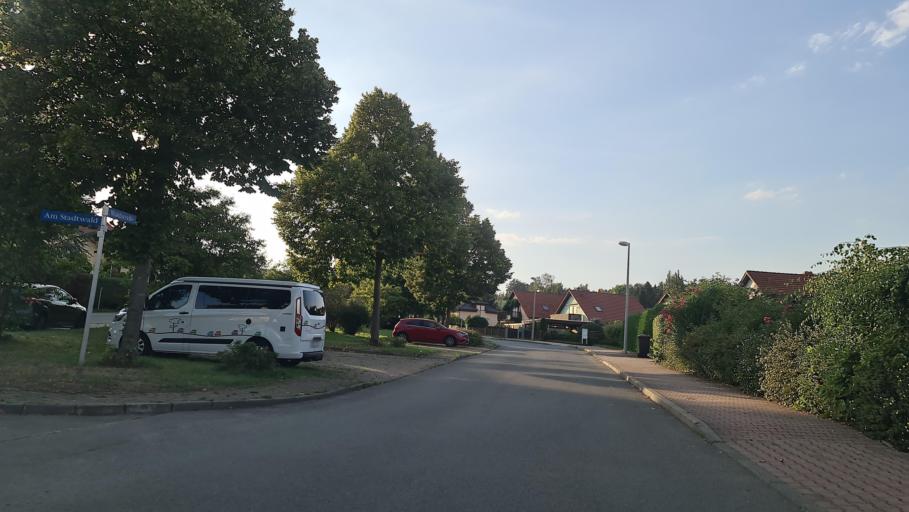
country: DE
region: Saxony
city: Lichtentanne
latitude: 50.7269
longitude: 12.4347
